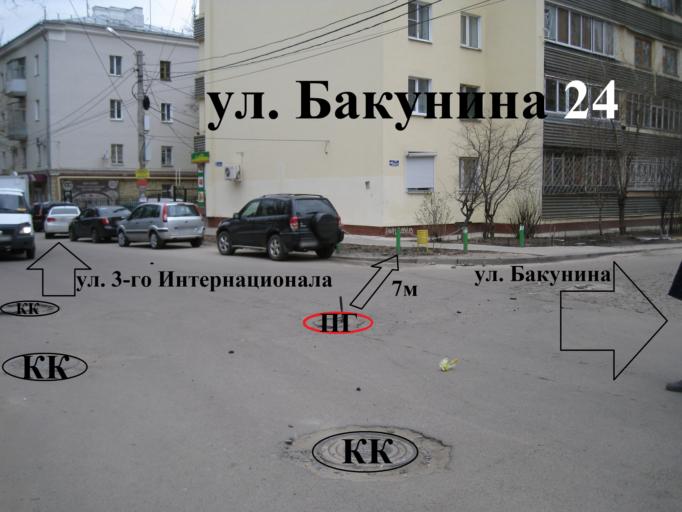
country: RU
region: Voronezj
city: Voronezh
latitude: 51.6718
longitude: 39.1856
